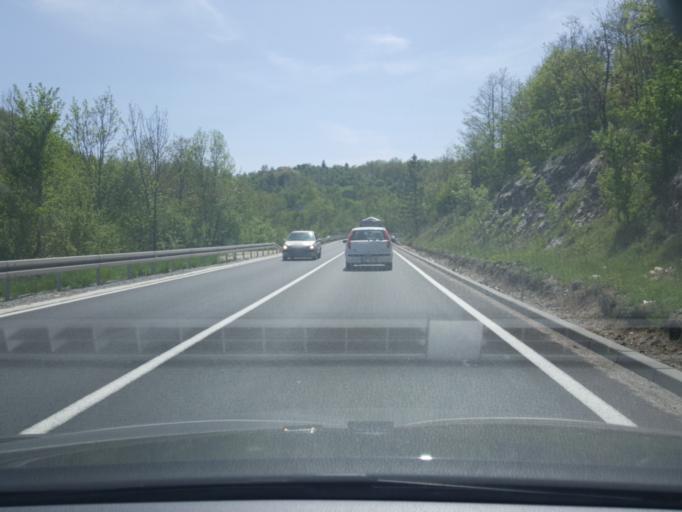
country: RS
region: Central Serbia
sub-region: Zlatiborski Okrug
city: Cajetina
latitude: 43.7840
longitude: 19.7512
